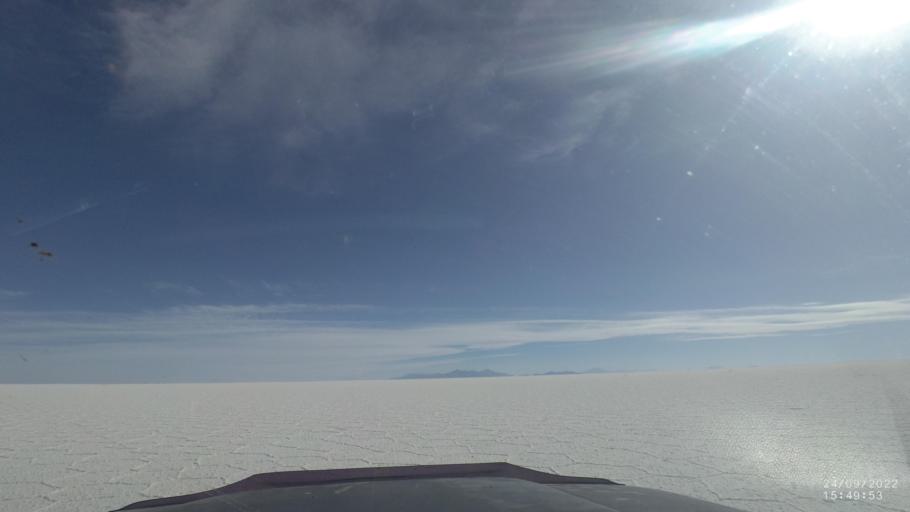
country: BO
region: Potosi
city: Colchani
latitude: -20.3045
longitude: -67.2452
